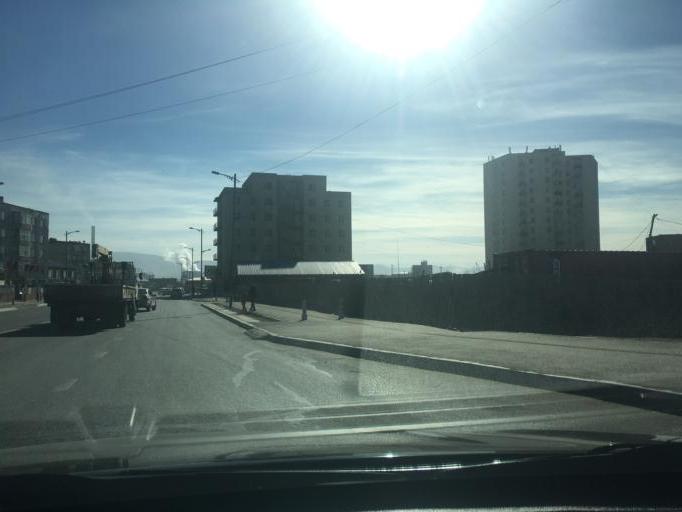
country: MN
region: Ulaanbaatar
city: Ulaanbaatar
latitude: 47.9127
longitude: 106.7826
